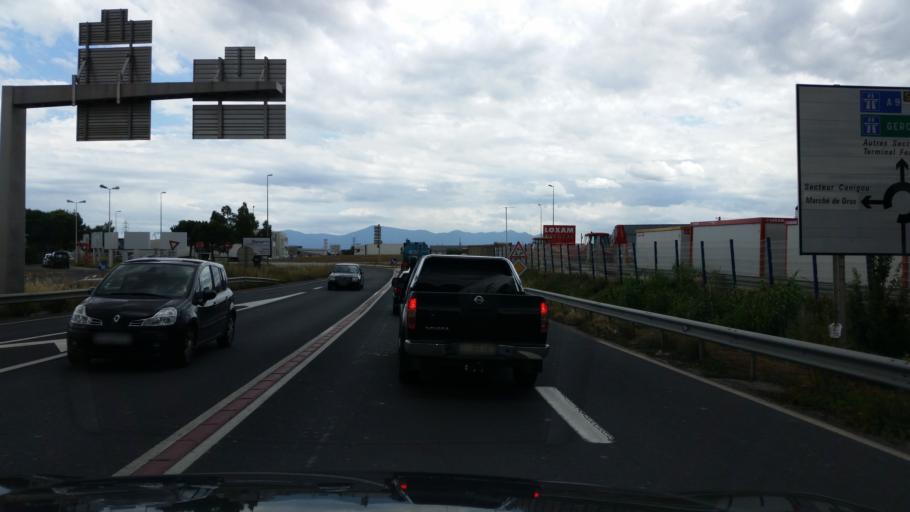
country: FR
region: Languedoc-Roussillon
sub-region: Departement des Pyrenees-Orientales
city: Saint-Esteve
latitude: 42.6921
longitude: 2.8515
